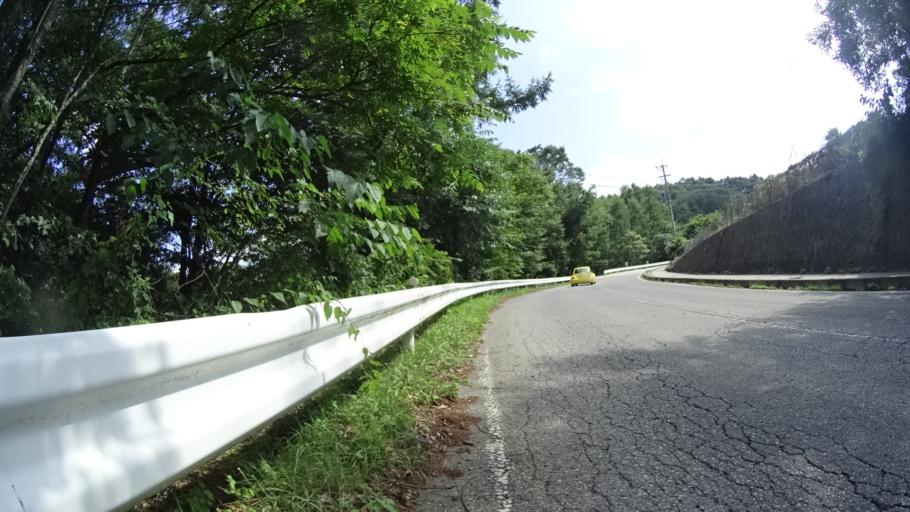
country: JP
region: Nagano
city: Saku
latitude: 36.0576
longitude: 138.4651
